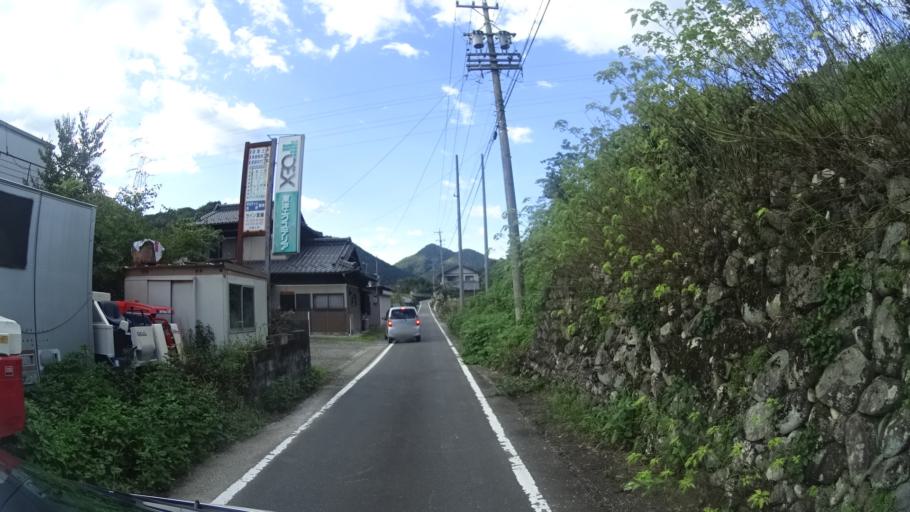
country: JP
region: Gifu
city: Minokamo
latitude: 35.5260
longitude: 137.1165
